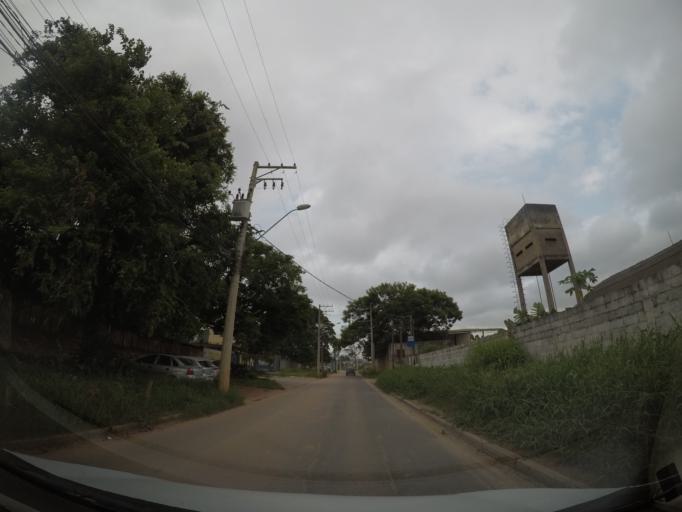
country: BR
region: Sao Paulo
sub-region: Aruja
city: Aruja
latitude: -23.4107
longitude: -46.3833
